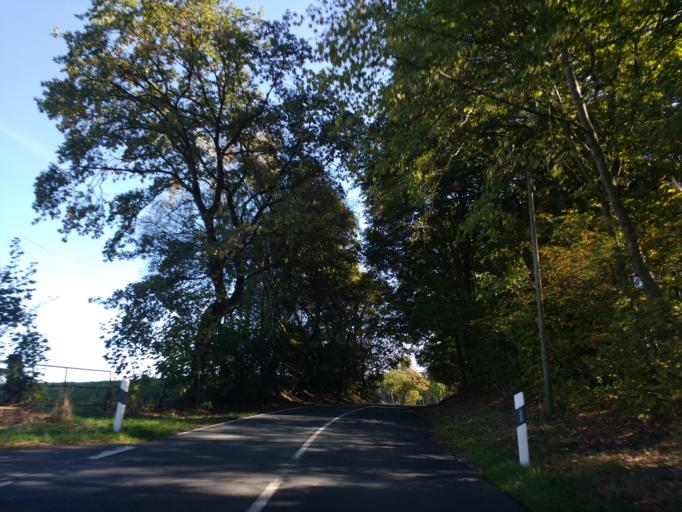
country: DE
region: North Rhine-Westphalia
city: Lichtenau
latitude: 51.6191
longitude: 8.9233
